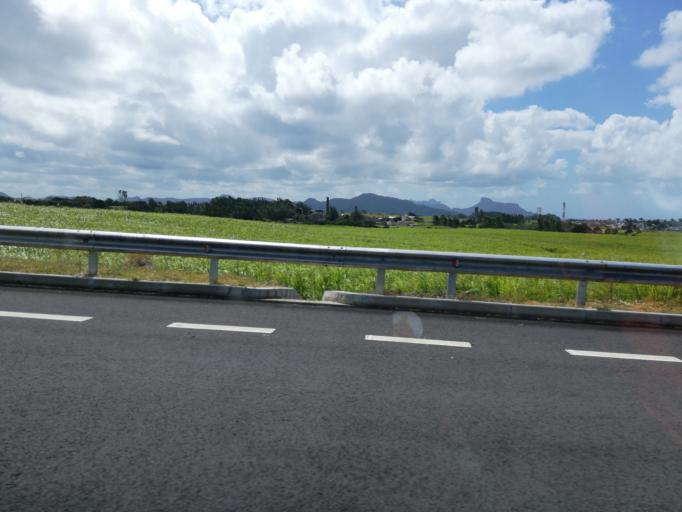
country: MU
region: Grand Port
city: Plaine Magnien
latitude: -20.4337
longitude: 57.6468
